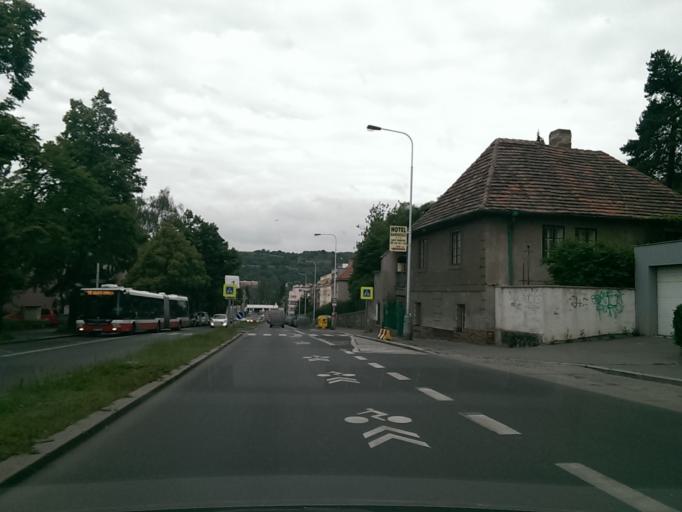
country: CZ
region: Praha
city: Branik
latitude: 50.0456
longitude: 14.4198
